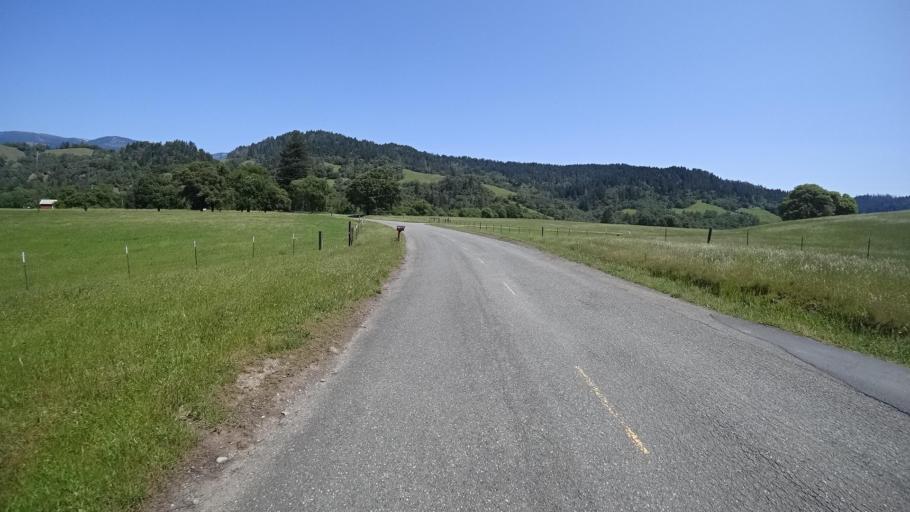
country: US
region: California
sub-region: Humboldt County
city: Redway
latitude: 40.2165
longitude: -123.6390
